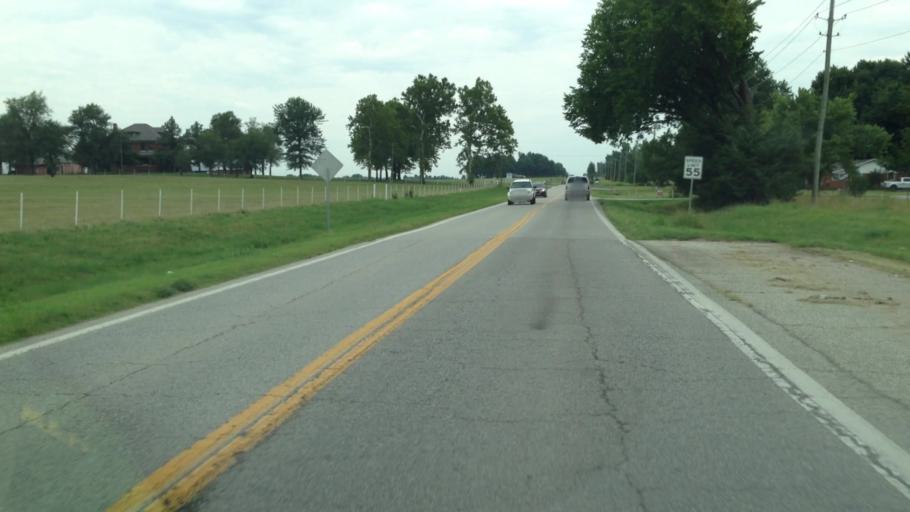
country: US
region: Oklahoma
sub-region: Craig County
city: Vinita
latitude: 36.6589
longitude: -95.1436
